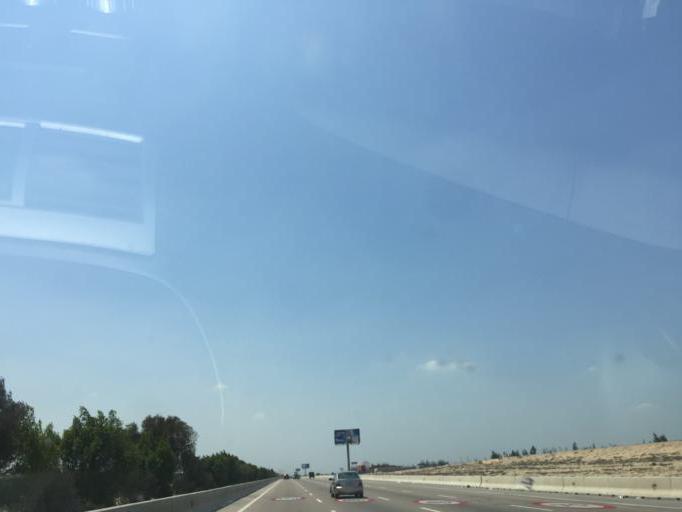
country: EG
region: Al Buhayrah
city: Beheira
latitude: 30.4481
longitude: 30.3191
